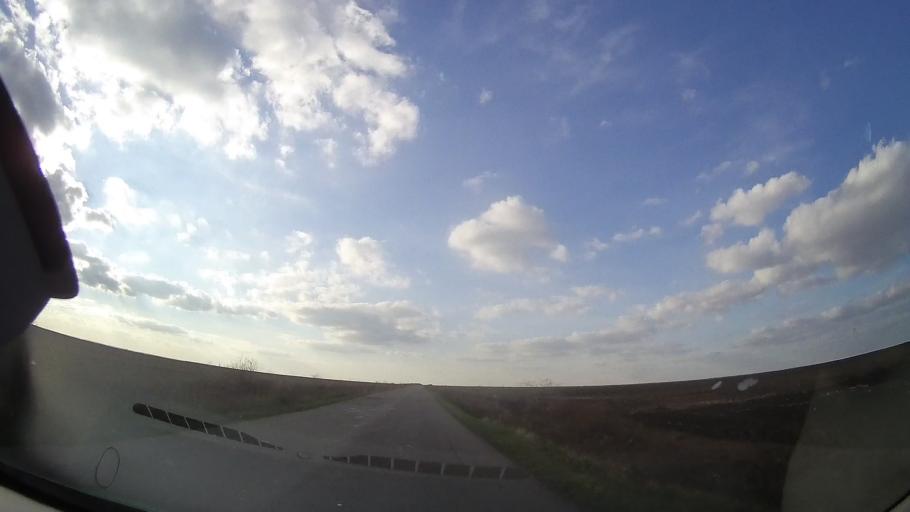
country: RO
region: Constanta
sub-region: Comuna Cerchezu
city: Cerchezu
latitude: 43.8233
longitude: 28.1482
